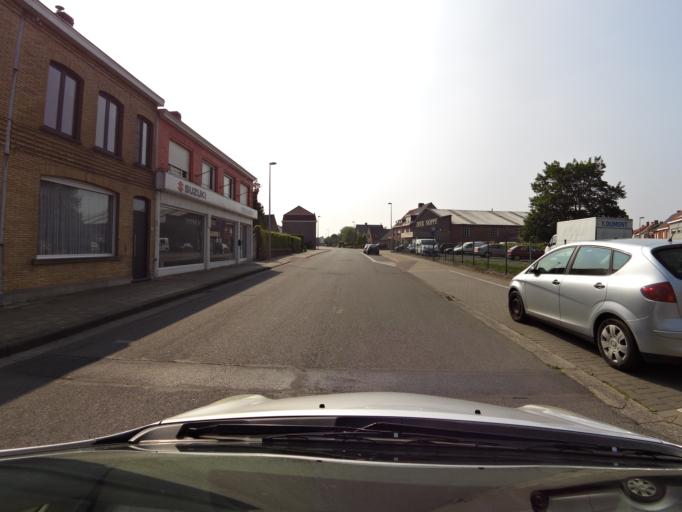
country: BE
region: Flanders
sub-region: Provincie West-Vlaanderen
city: Poperinge
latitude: 50.8557
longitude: 2.7163
